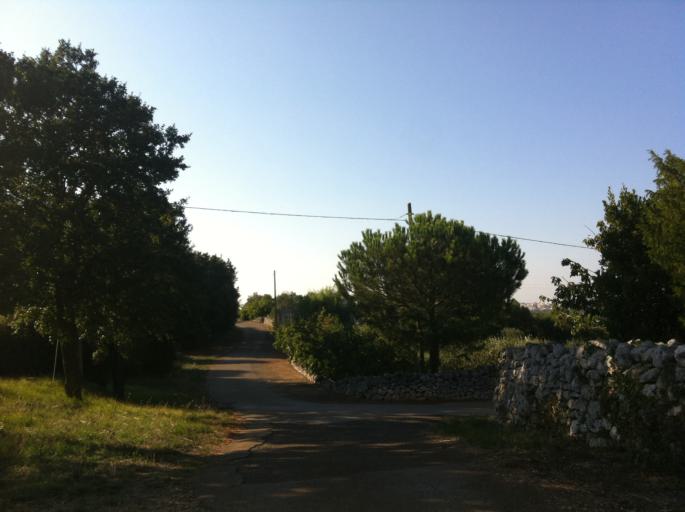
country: IT
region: Apulia
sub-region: Provincia di Bari
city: Putignano
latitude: 40.8259
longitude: 17.1392
